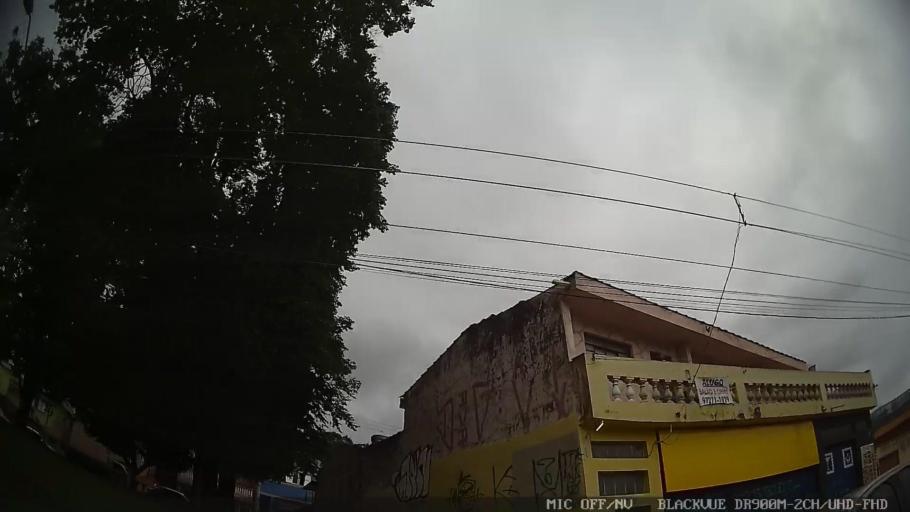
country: BR
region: Sao Paulo
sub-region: Osasco
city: Osasco
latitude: -23.4917
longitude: -46.7457
